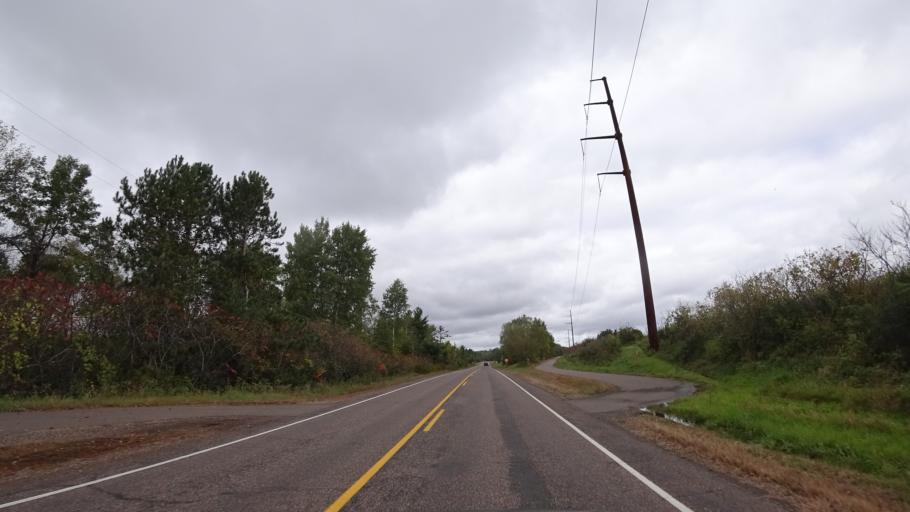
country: US
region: Wisconsin
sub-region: Chippewa County
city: Lake Wissota
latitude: 45.0253
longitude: -91.2869
